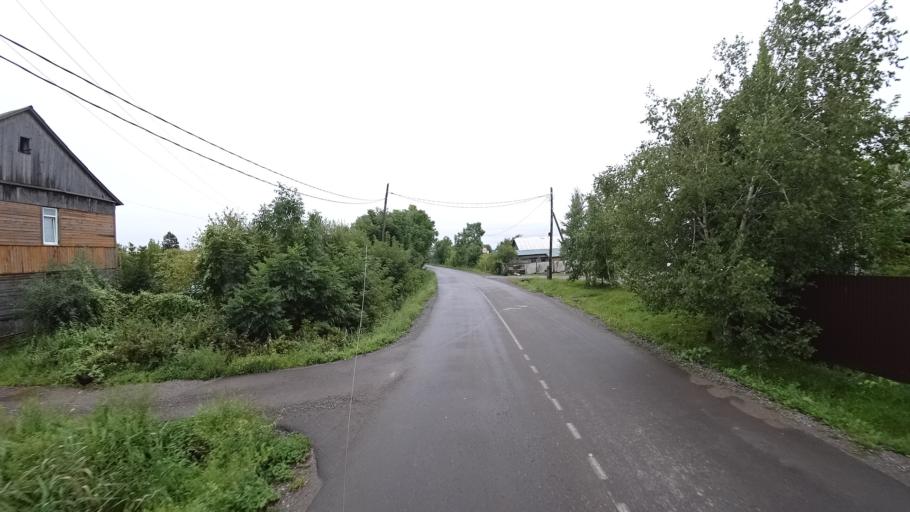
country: RU
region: Primorskiy
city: Monastyrishche
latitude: 44.2069
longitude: 132.4357
